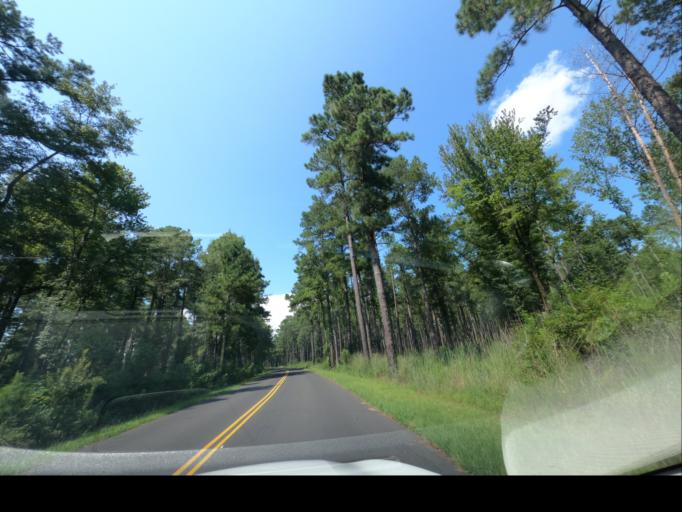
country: US
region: South Carolina
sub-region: Richland County
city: Gadsden
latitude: 33.8375
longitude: -80.8290
